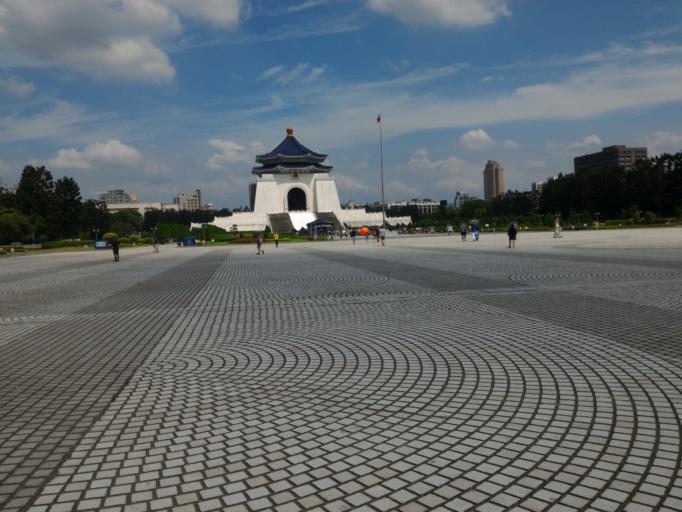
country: TW
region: Taipei
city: Taipei
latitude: 25.0365
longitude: 121.5187
